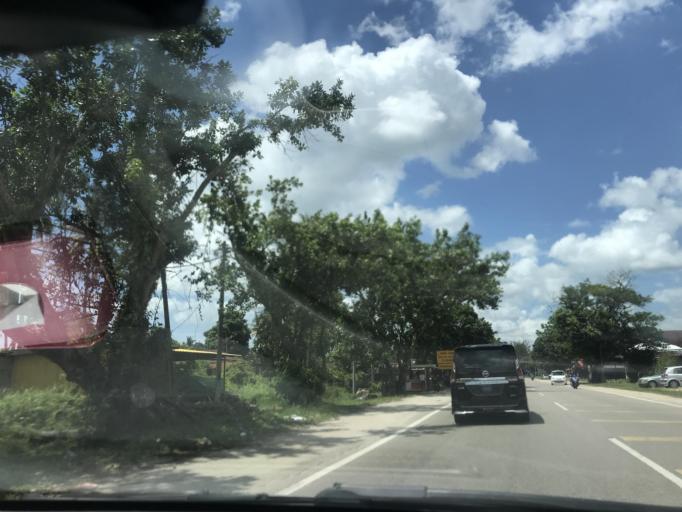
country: TH
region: Narathiwat
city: Tak Bai
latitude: 6.2264
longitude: 102.0973
